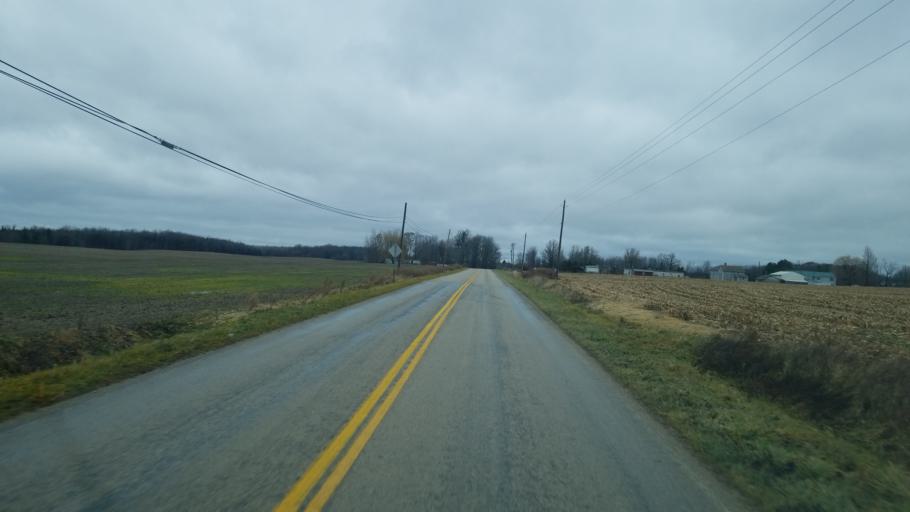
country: US
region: Ohio
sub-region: Ashtabula County
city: Andover
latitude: 41.6484
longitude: -80.6161
